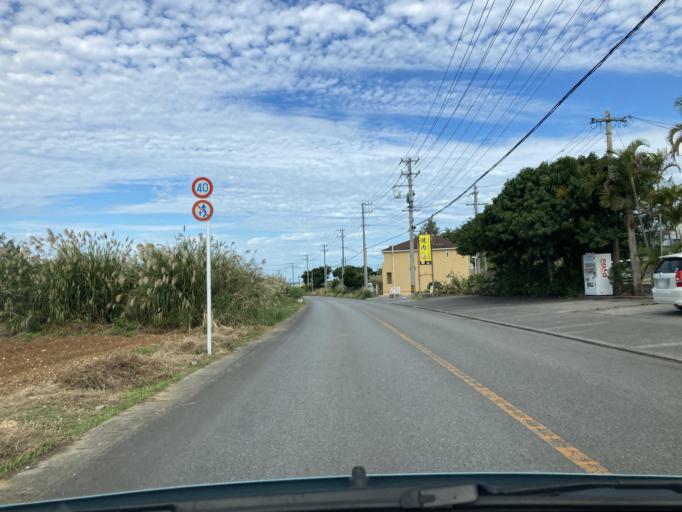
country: JP
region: Okinawa
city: Ishikawa
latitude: 26.4292
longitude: 127.7292
